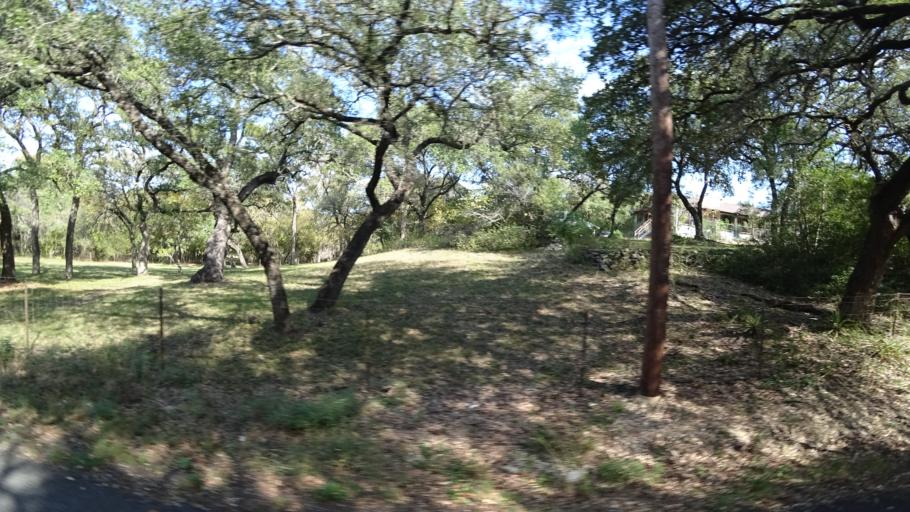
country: US
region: Texas
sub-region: Travis County
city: Barton Creek
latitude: 30.2227
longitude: -97.9239
